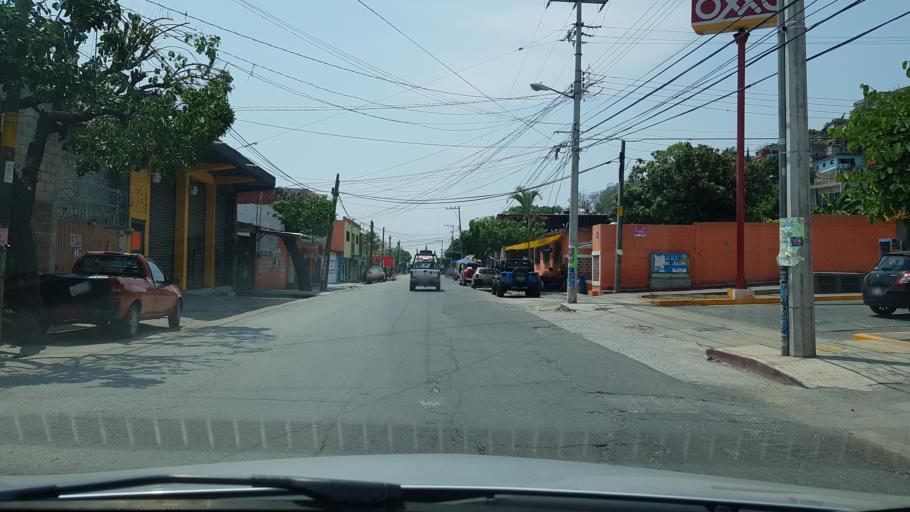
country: MX
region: Morelos
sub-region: Jiutepec
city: Jiutepec
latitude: 18.8759
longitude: -99.1727
